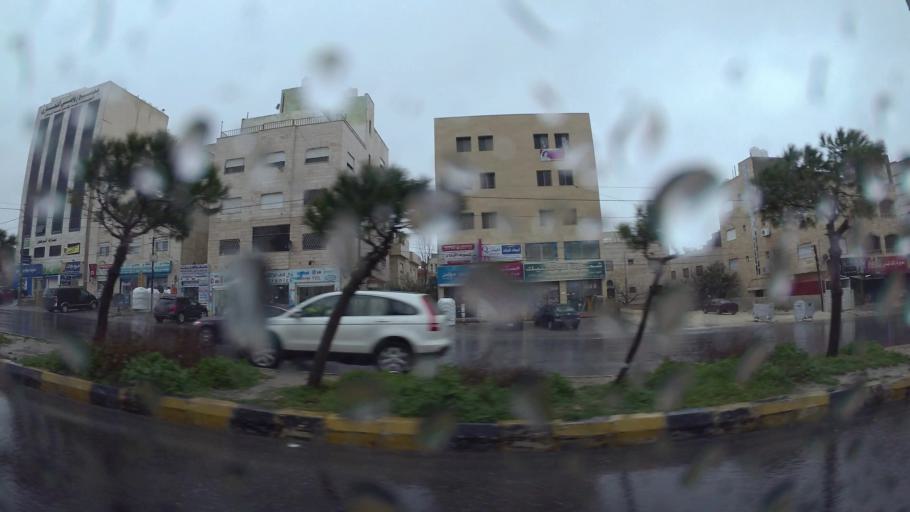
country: JO
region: Amman
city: Al Jubayhah
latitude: 32.0493
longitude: 35.8867
